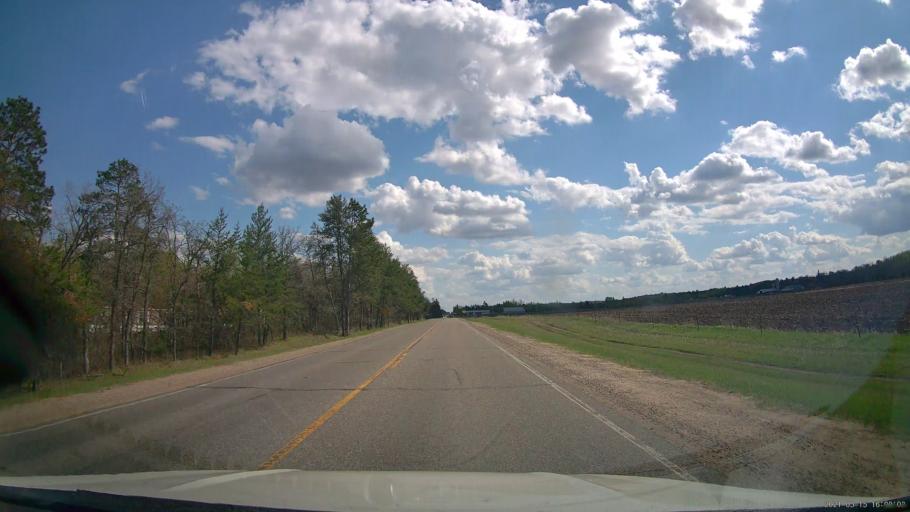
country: US
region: Minnesota
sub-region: Hubbard County
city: Park Rapids
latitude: 46.9628
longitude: -94.9526
